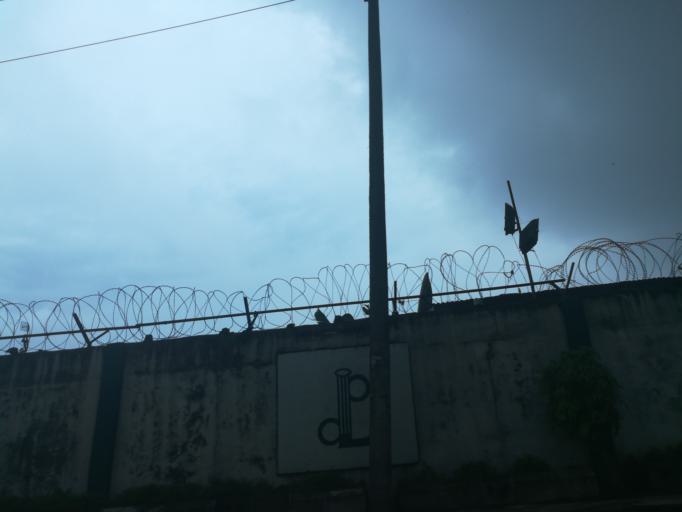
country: NG
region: Lagos
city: Agege
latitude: 6.6137
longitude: 3.3308
